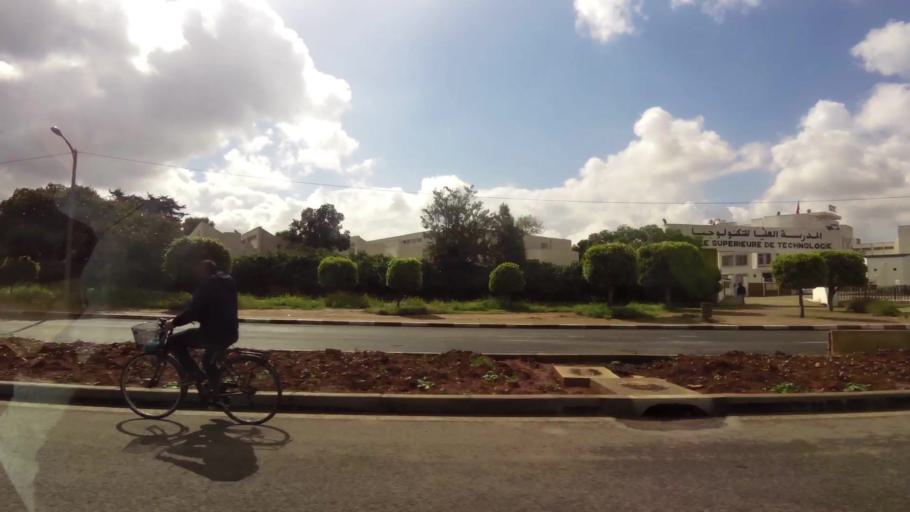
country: MA
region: Grand Casablanca
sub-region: Casablanca
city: Casablanca
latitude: 33.5419
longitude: -7.6562
